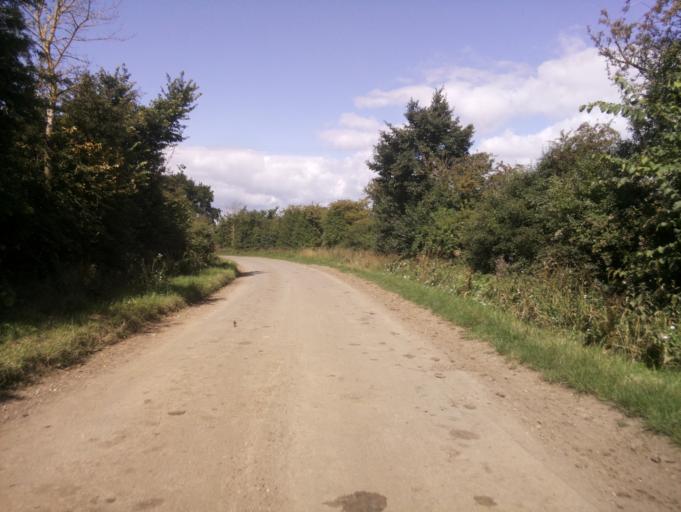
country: GB
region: England
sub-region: Milton Keynes
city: Calverton
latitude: 51.9963
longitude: -0.8758
